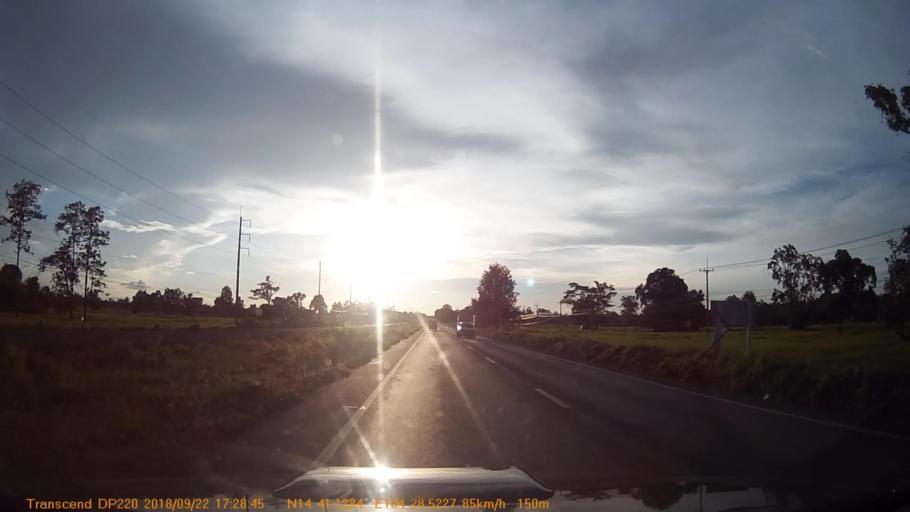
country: TH
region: Sisaket
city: Khun Han
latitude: 14.6855
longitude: 104.4750
